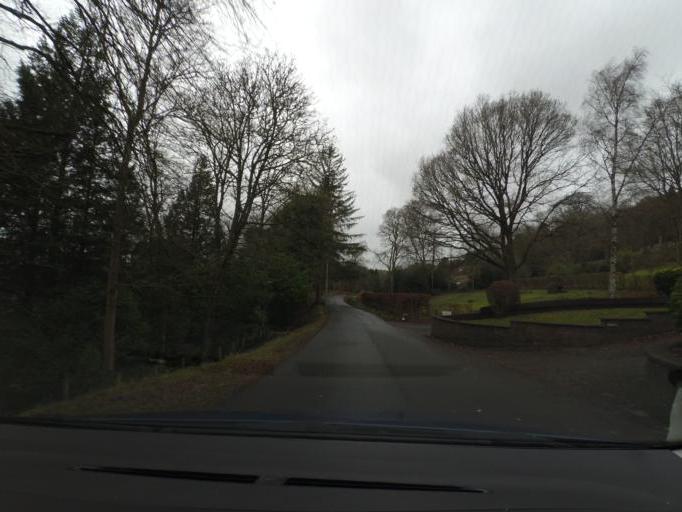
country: GB
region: Scotland
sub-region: The Scottish Borders
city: Hawick
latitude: 55.4233
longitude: -2.7994
